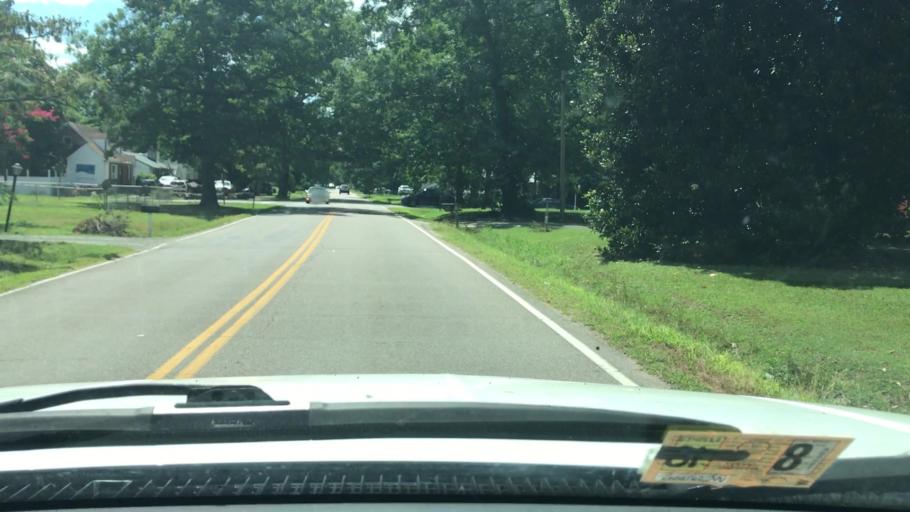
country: US
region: Virginia
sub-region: Henrico County
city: East Highland Park
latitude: 37.5733
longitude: -77.4016
